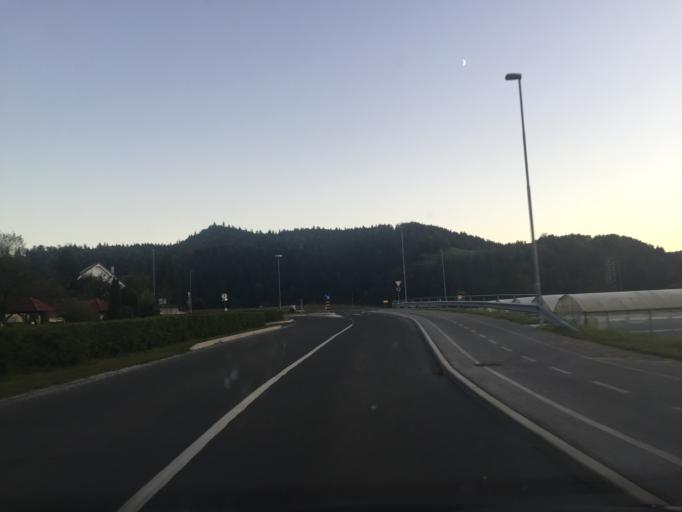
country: SI
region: Sostanj
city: Sostanj
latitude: 46.3866
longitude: 15.0372
